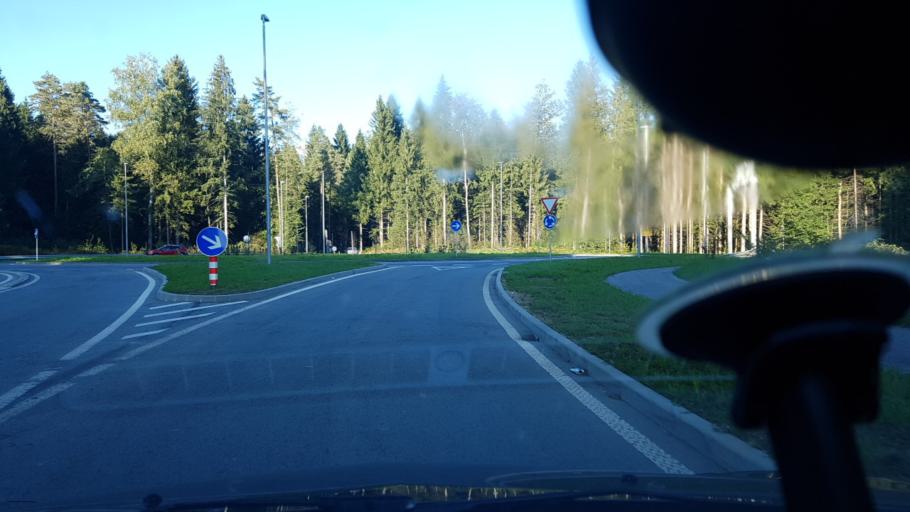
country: SI
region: Cerklje na Gorenjskem
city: Cerklje na Gorenjskem
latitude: 46.2341
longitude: 14.4598
